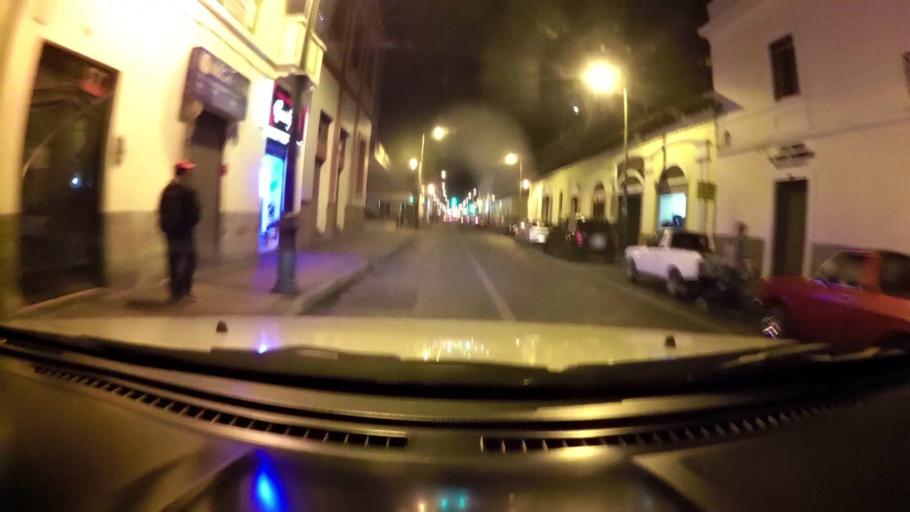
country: EC
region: Chimborazo
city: Riobamba
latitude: -1.6739
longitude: -78.6473
